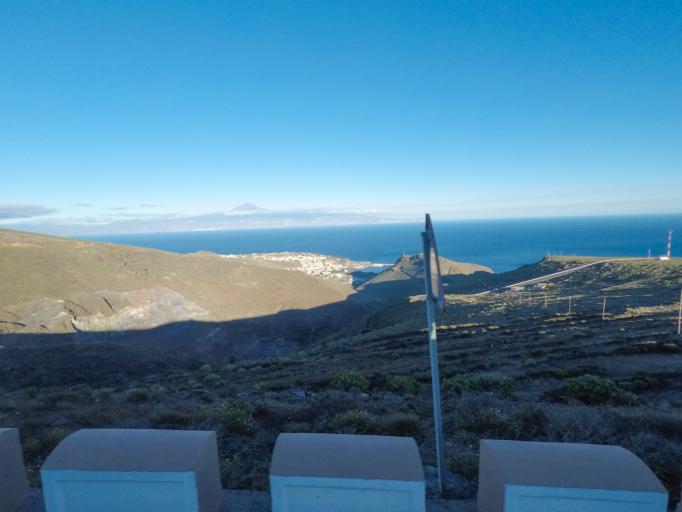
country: ES
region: Canary Islands
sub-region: Provincia de Santa Cruz de Tenerife
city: San Sebastian de la Gomera
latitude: 28.0863
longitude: -17.1420
